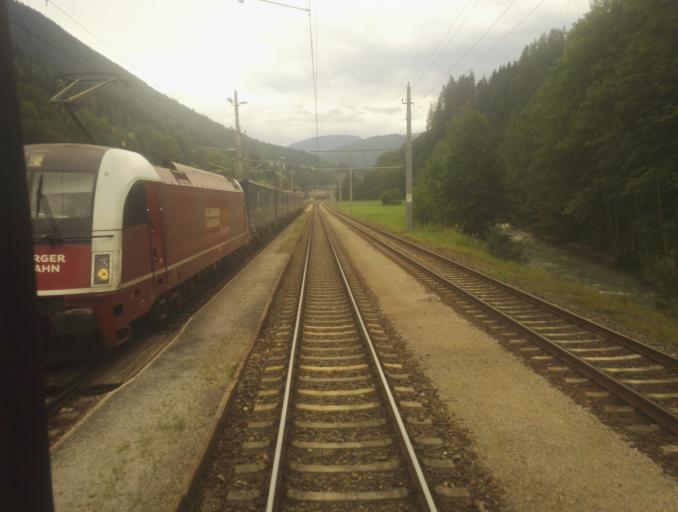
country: AT
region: Salzburg
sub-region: Politischer Bezirk Sankt Johann im Pongau
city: Huttau
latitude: 47.4157
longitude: 13.3208
